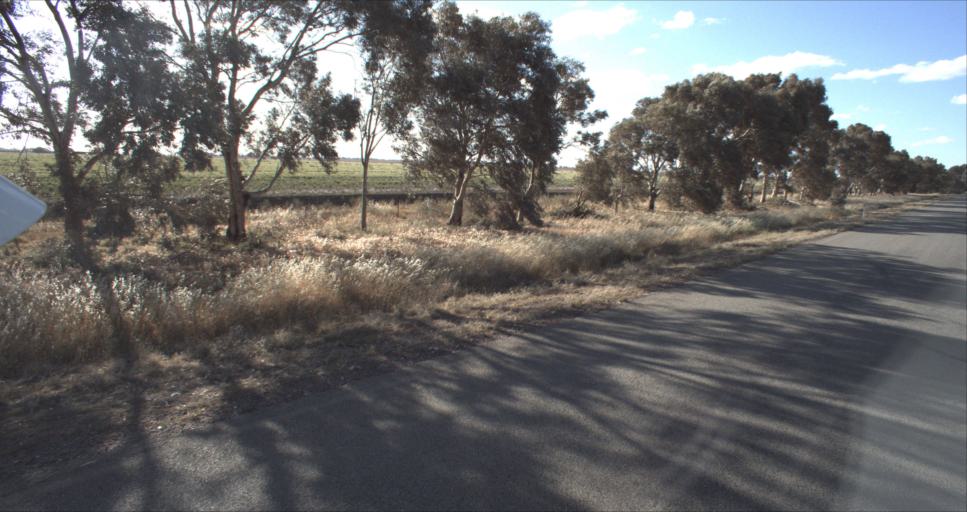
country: AU
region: New South Wales
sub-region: Leeton
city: Leeton
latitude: -34.5458
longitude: 146.2795
